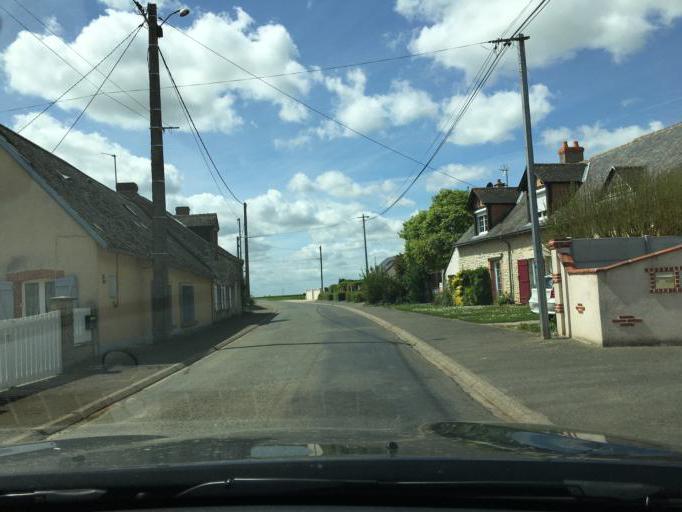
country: FR
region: Centre
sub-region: Departement du Loiret
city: Bricy
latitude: 48.0529
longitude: 1.7865
